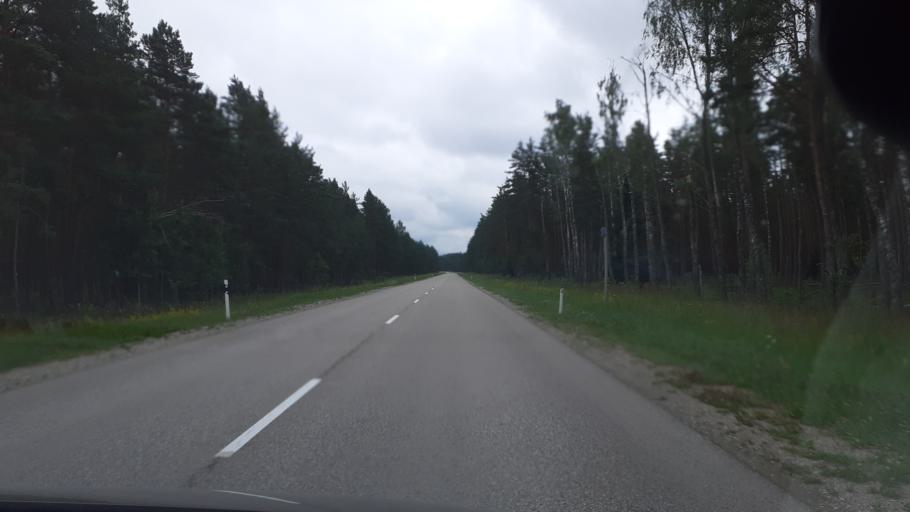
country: LV
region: Ventspils Rajons
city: Piltene
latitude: 57.1249
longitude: 21.7388
